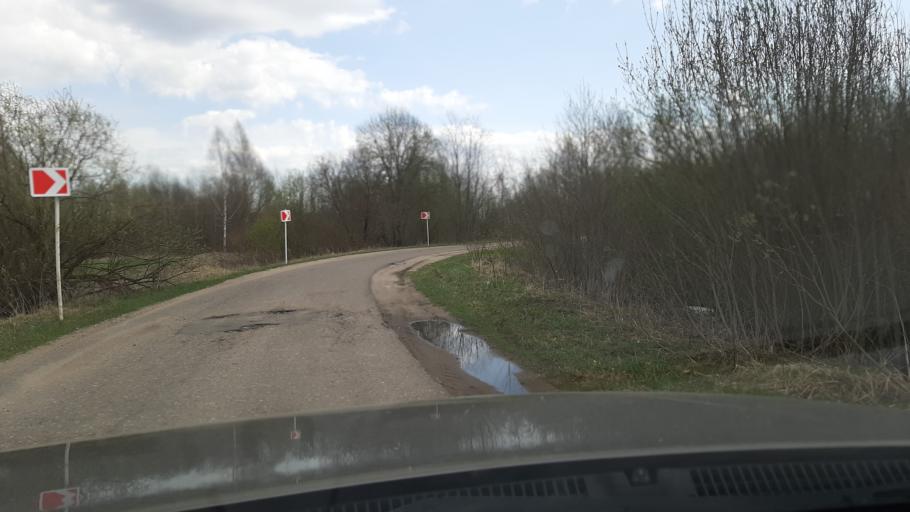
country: RU
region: Ivanovo
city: Furmanov
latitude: 57.3017
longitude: 41.1655
